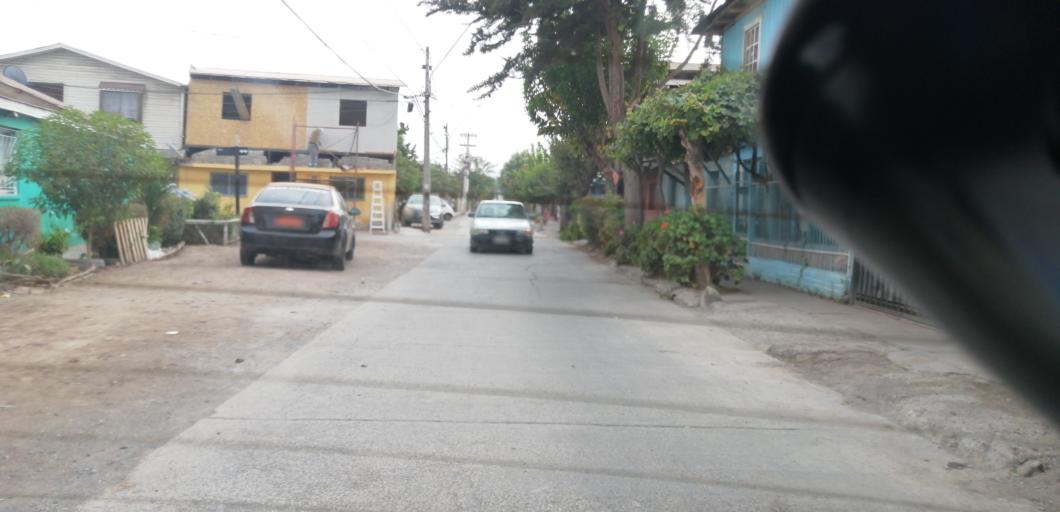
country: CL
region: Santiago Metropolitan
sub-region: Provincia de Santiago
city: Lo Prado
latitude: -33.4359
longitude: -70.7478
